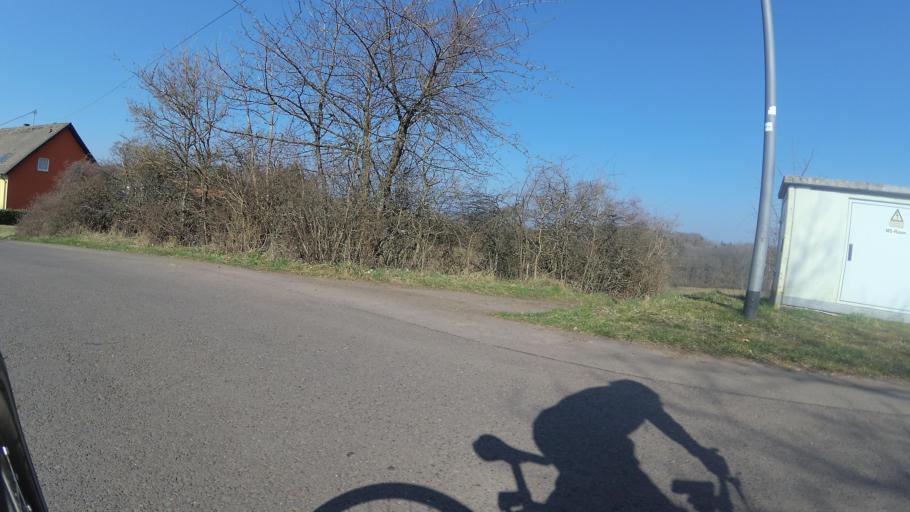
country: DE
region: Rheinland-Pfalz
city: Ruckweiler
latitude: 49.5835
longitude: 7.2373
